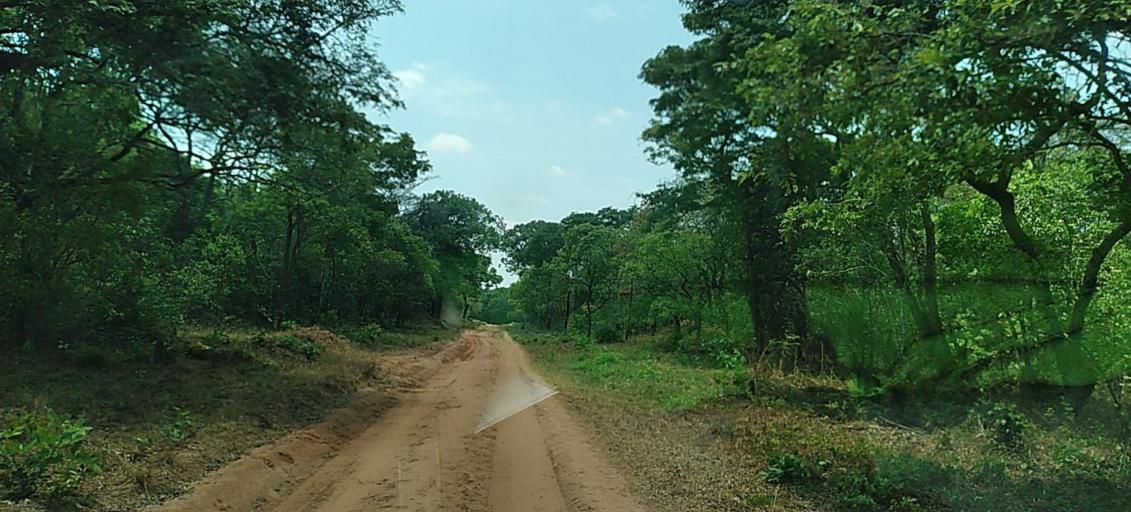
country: CD
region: Katanga
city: Kolwezi
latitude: -11.3518
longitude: 25.2128
